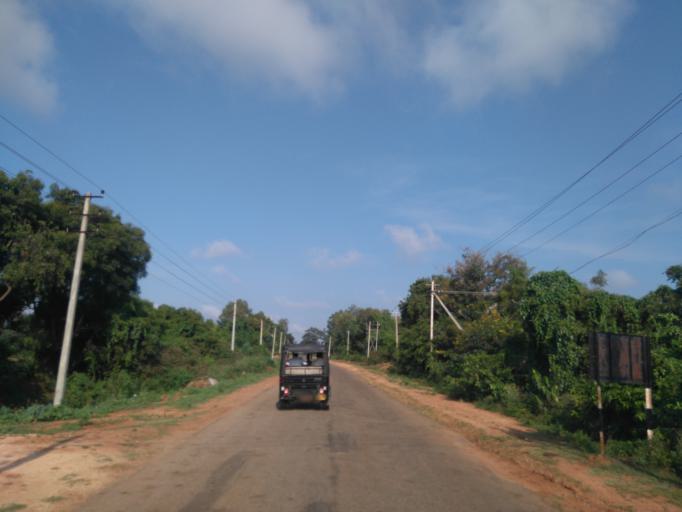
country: IN
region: Karnataka
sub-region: Chamrajnagar
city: Kollegal
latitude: 12.2567
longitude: 77.0599
